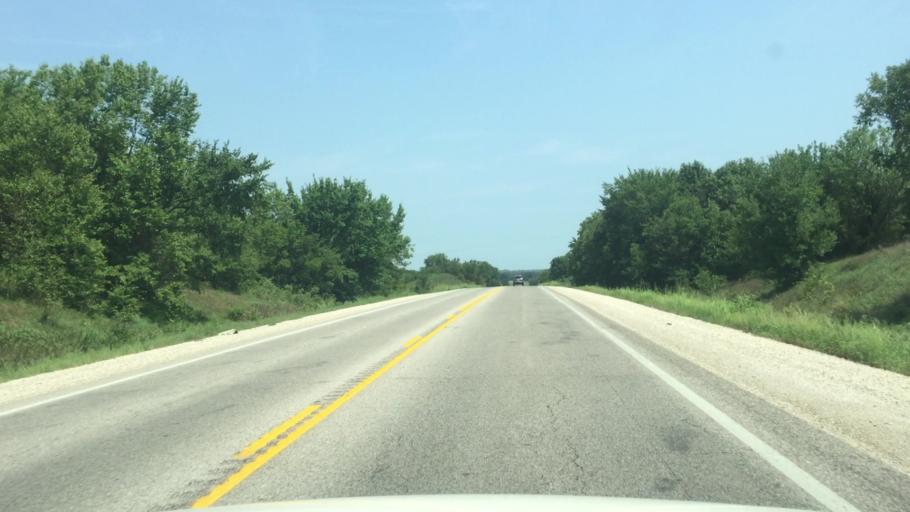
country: US
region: Kansas
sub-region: Montgomery County
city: Cherryvale
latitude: 37.1575
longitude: -95.5768
